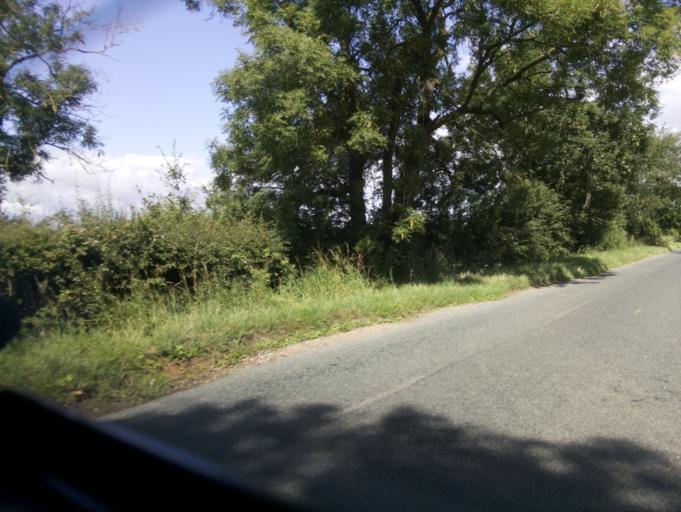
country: GB
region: England
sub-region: Milton Keynes
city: Calverton
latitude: 51.9938
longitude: -0.8604
